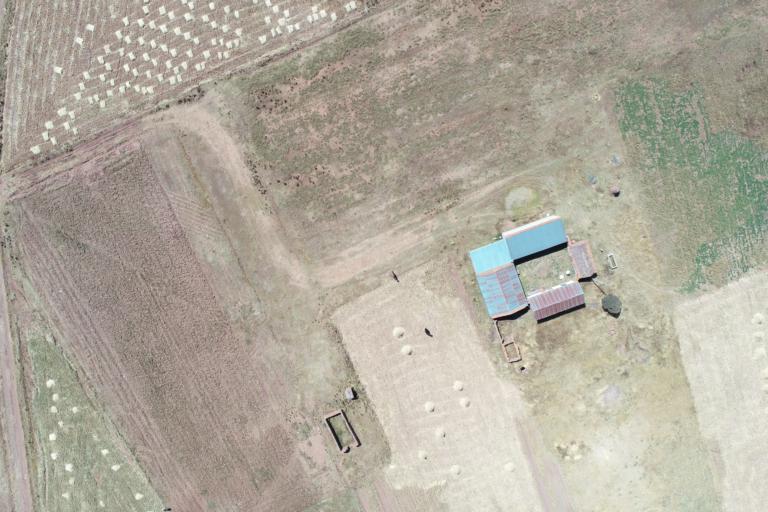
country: BO
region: La Paz
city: Tiahuanaco
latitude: -16.5896
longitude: -68.7701
